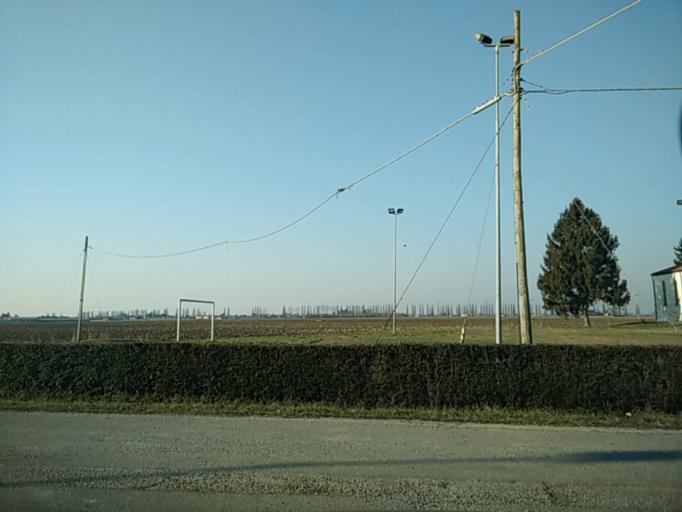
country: IT
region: Veneto
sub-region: Provincia di Venezia
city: Torre di Mosto
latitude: 45.6838
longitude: 12.7427
